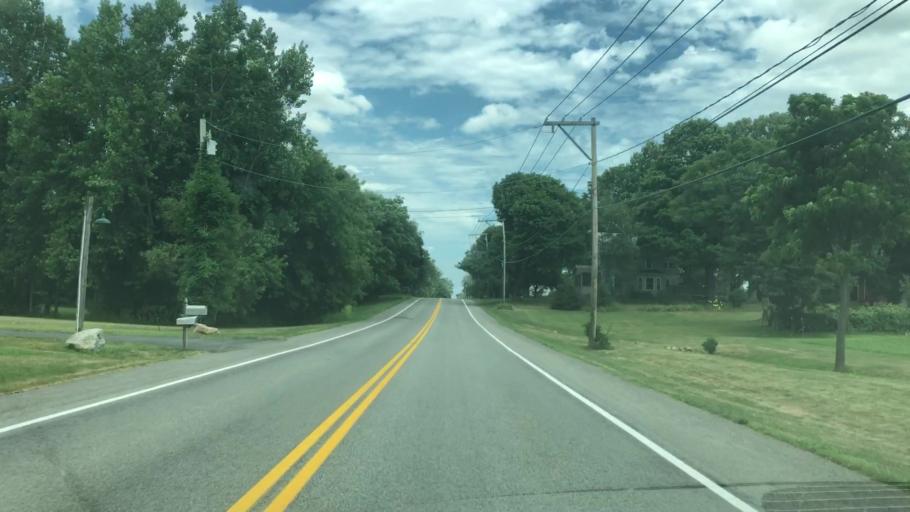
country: US
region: New York
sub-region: Monroe County
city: Fairport
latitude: 43.1381
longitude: -77.4005
